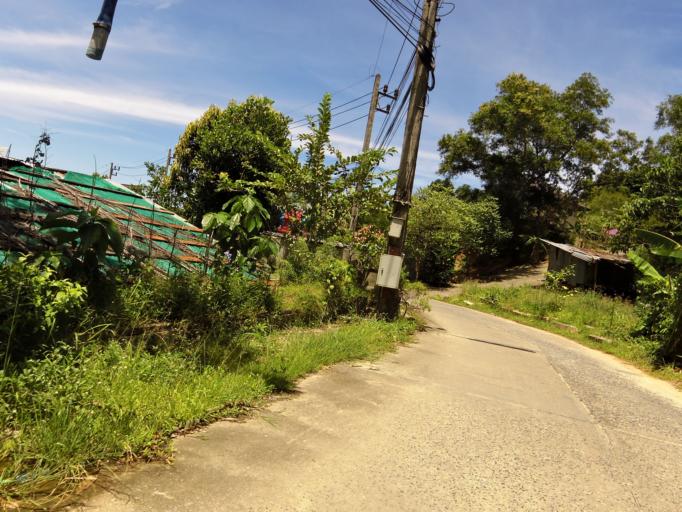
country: TH
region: Phuket
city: Ban Karon
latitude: 7.8499
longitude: 98.3035
